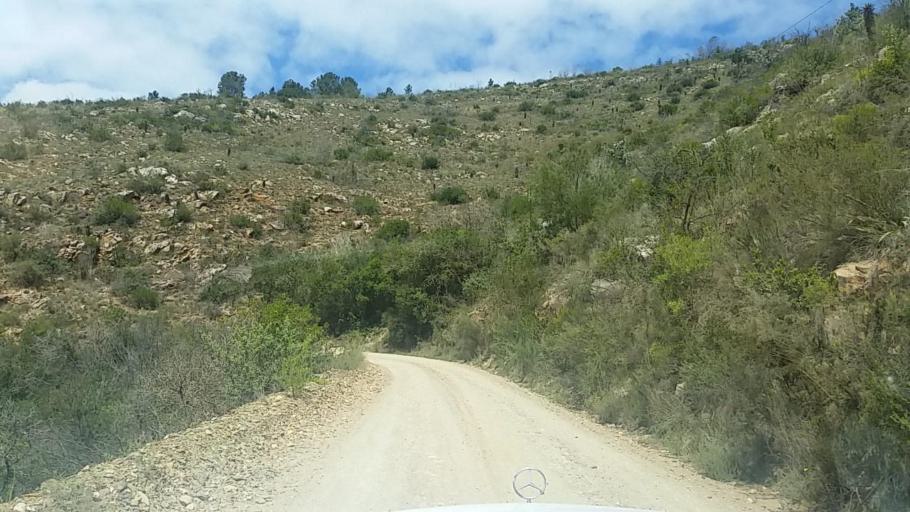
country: ZA
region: Western Cape
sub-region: Eden District Municipality
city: Knysna
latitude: -33.8257
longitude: 23.1840
